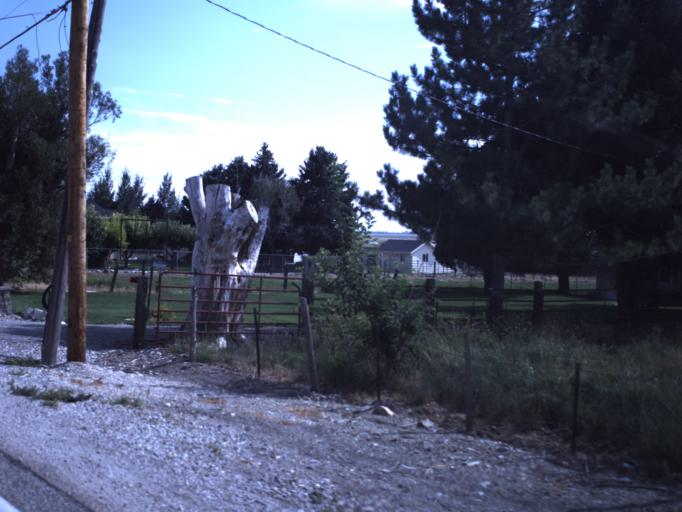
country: US
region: Utah
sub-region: Box Elder County
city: Honeyville
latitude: 41.6083
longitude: -112.0604
